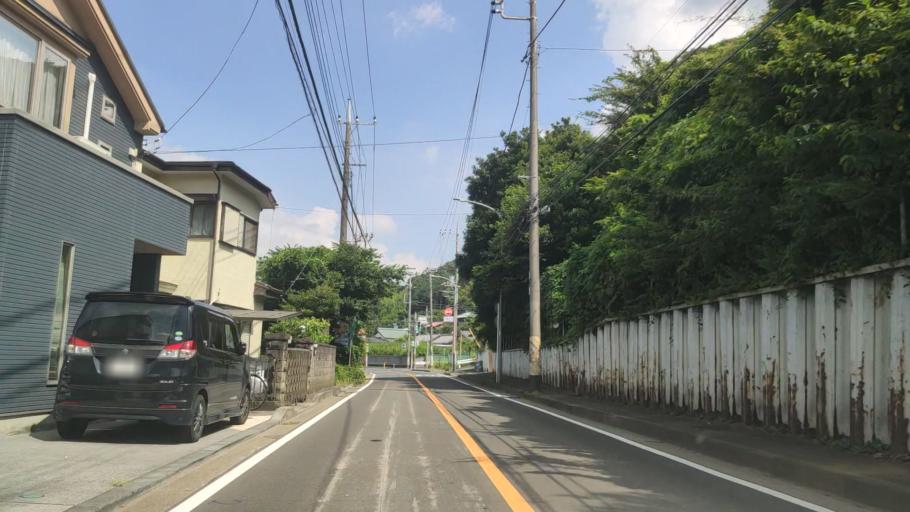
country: JP
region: Kanagawa
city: Minami-rinkan
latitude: 35.4419
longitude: 139.5074
